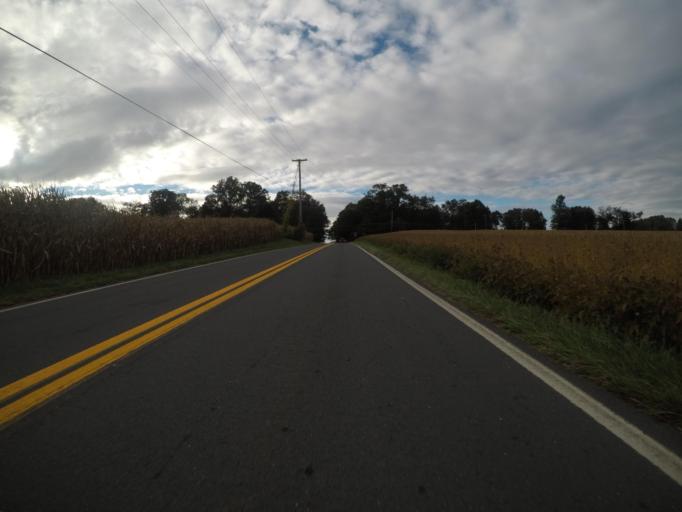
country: US
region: Maryland
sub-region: Carroll County
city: Hampstead
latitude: 39.5738
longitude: -76.8769
